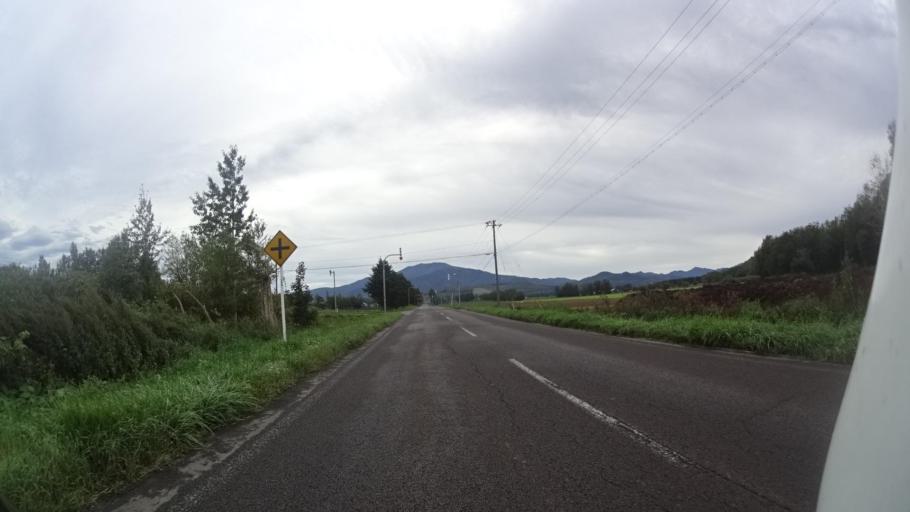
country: JP
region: Hokkaido
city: Shibetsu
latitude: 43.8735
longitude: 144.7243
